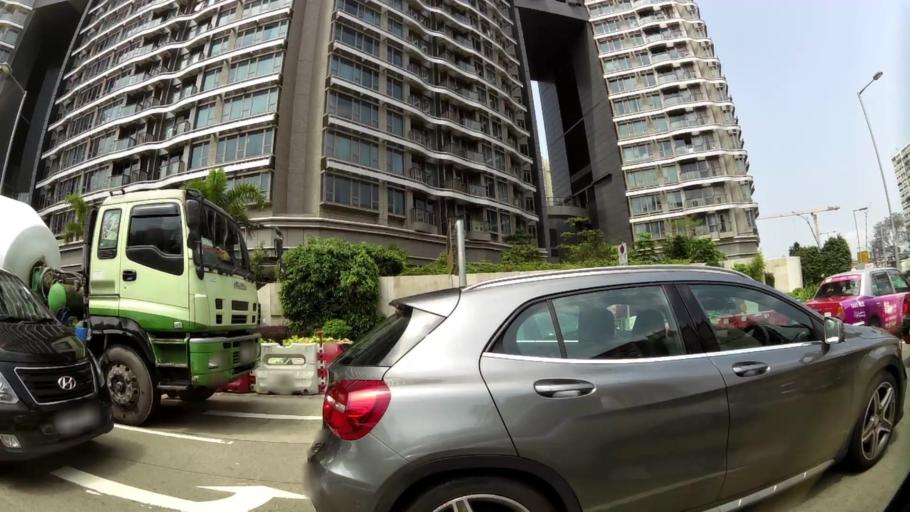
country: HK
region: Kowloon City
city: Kowloon
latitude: 22.3055
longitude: 114.1667
